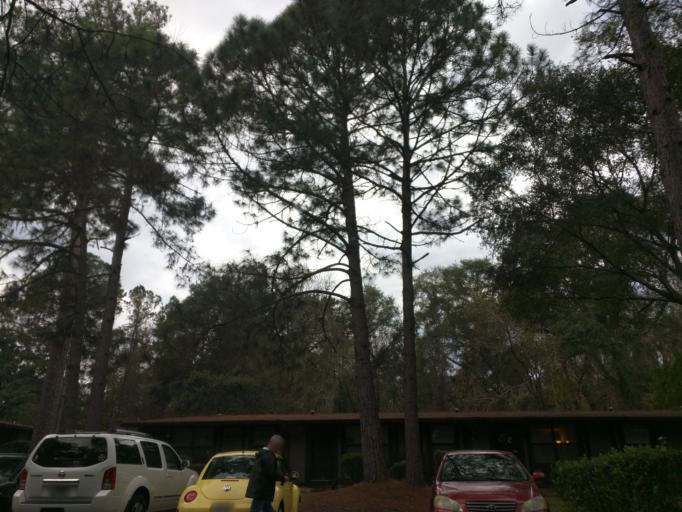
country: US
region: Florida
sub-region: Leon County
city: Tallahassee
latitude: 30.4343
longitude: -84.2466
